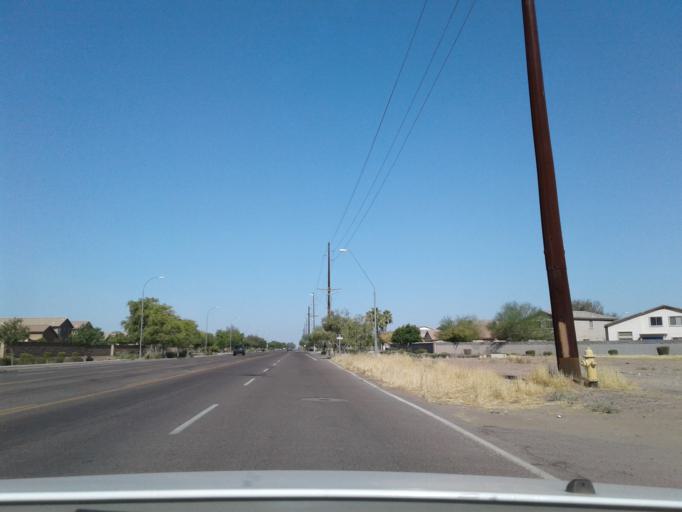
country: US
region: Arizona
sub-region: Maricopa County
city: Laveen
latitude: 33.3920
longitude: -112.1707
